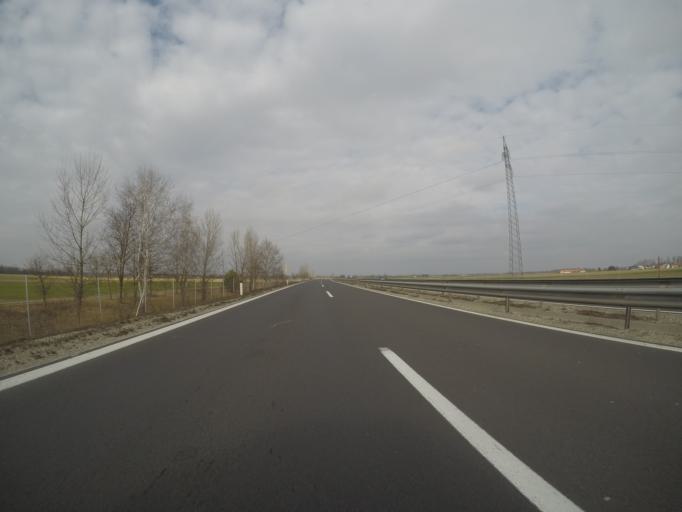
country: SI
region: Murska Sobota
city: Bakovci
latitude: 46.6208
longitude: 16.1333
